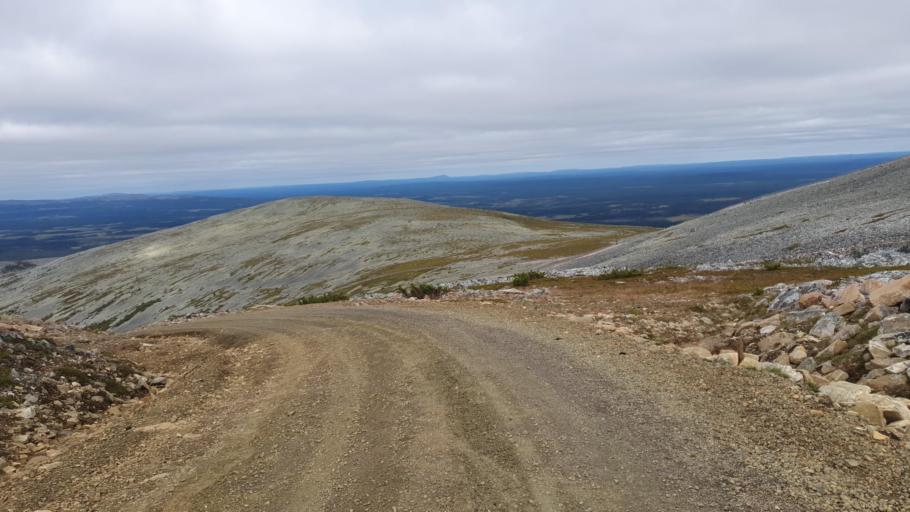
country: FI
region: Lapland
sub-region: Tunturi-Lappi
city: Kolari
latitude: 67.5694
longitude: 24.2137
